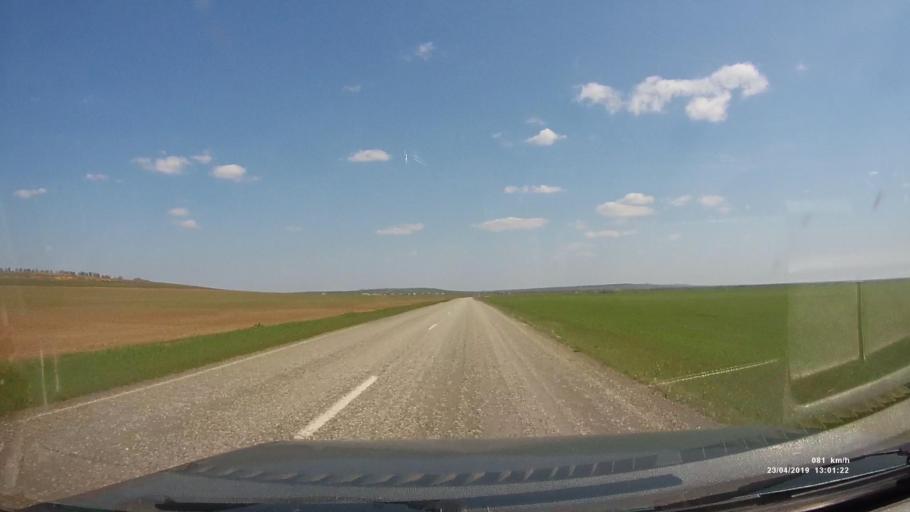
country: RU
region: Kalmykiya
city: Yashalta
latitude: 46.6039
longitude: 42.6510
